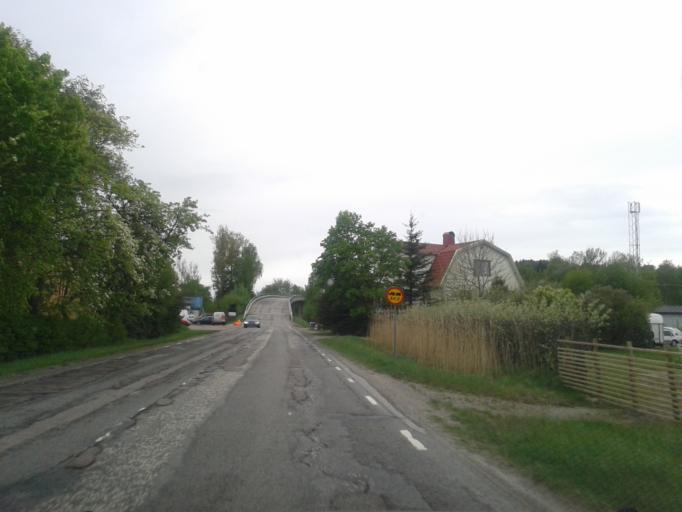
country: SE
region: Vaestra Goetaland
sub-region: Stenungsunds Kommun
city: Stora Hoga
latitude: 58.0188
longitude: 11.8378
